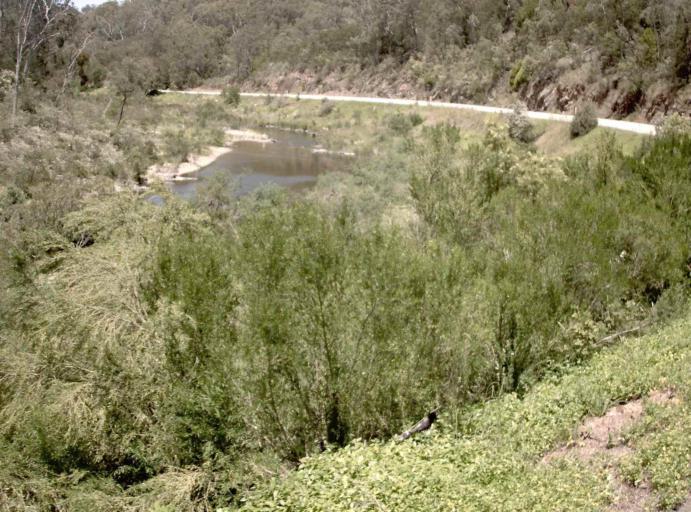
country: AU
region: Victoria
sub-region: East Gippsland
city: Bairnsdale
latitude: -37.4600
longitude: 147.8310
